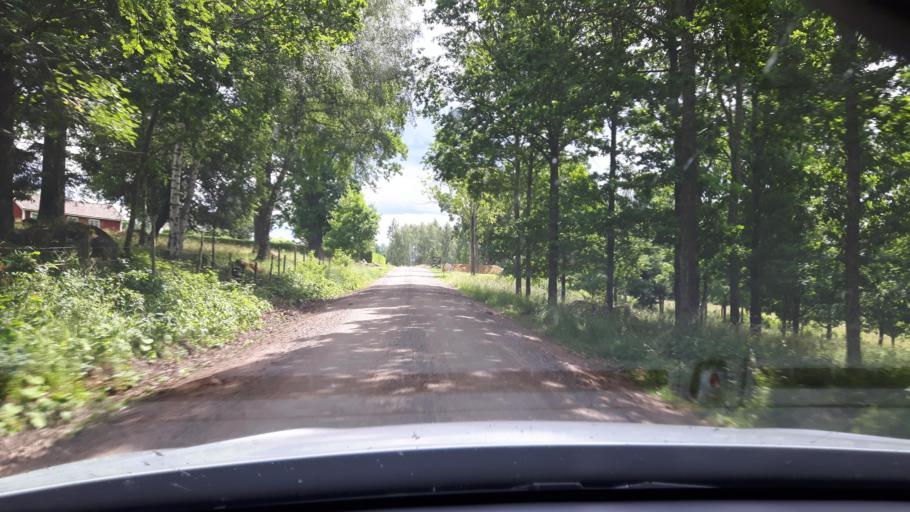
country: SE
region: OEstergoetland
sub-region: Kinda Kommun
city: Kisa
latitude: 58.0133
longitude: 15.6568
